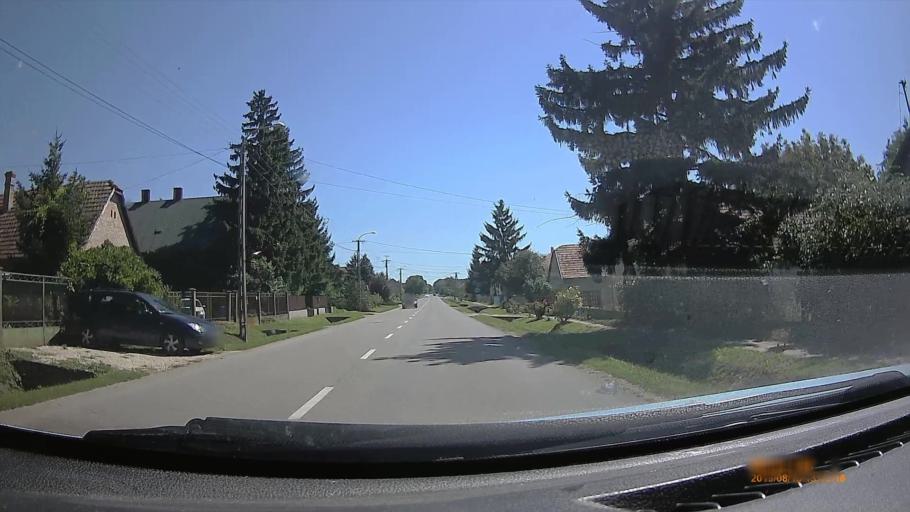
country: HU
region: Fejer
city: Cece
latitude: 46.7592
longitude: 18.6373
